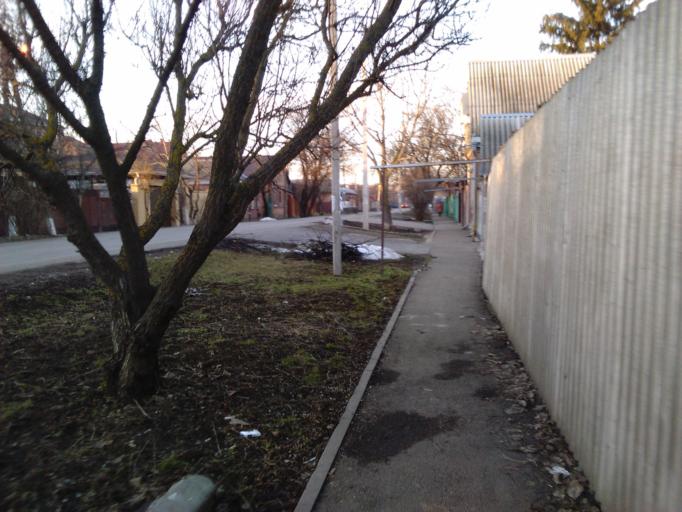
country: RU
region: Rostov
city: Bataysk
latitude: 47.1479
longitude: 39.7417
